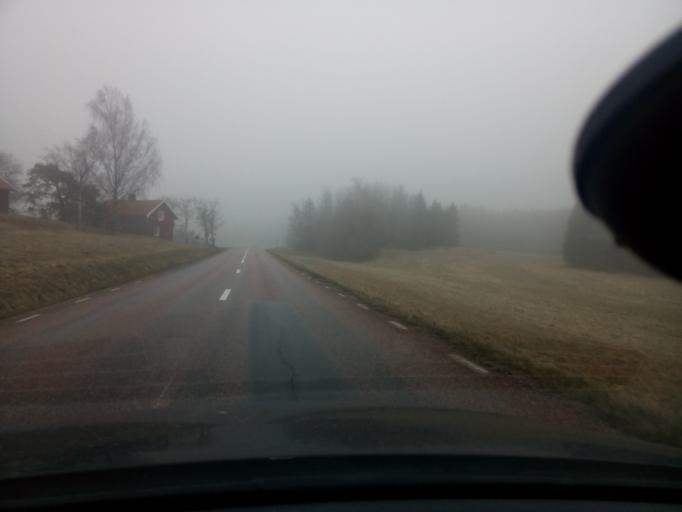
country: SE
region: Soedermanland
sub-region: Nykopings Kommun
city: Nykoping
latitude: 58.8359
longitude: 17.0717
